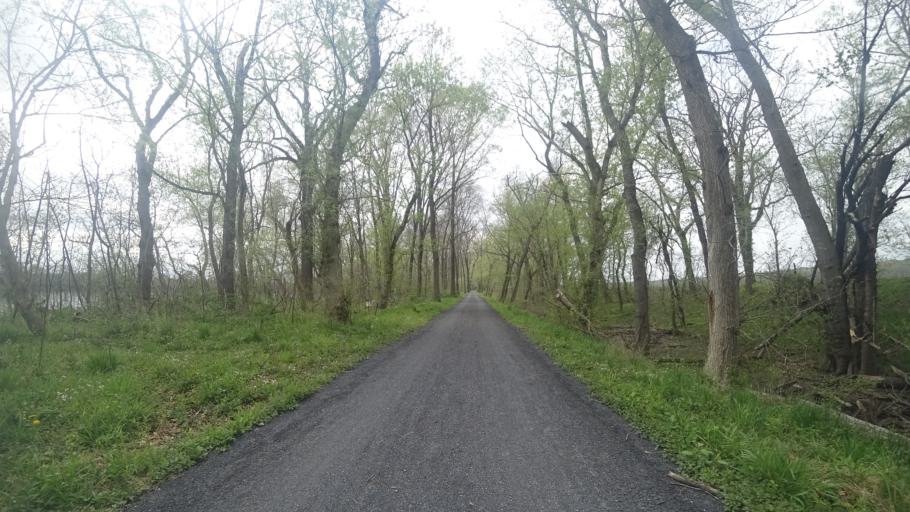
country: US
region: Virginia
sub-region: Loudoun County
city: University Center
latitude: 39.0780
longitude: -77.4376
